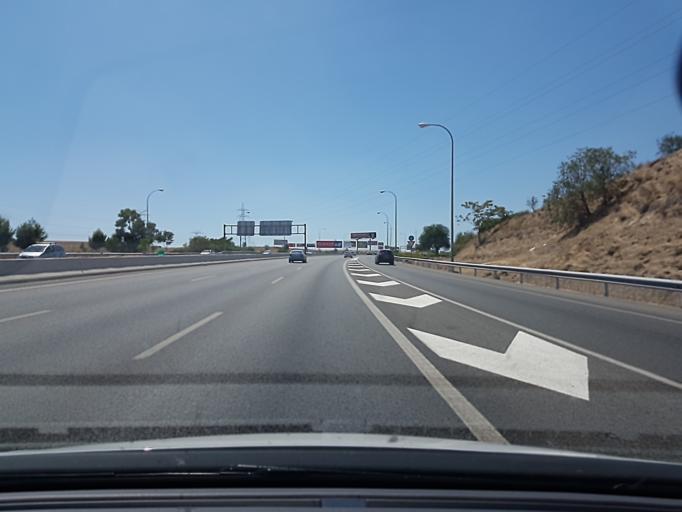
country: ES
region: Madrid
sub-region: Provincia de Madrid
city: Leganes
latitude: 40.3589
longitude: -3.7576
